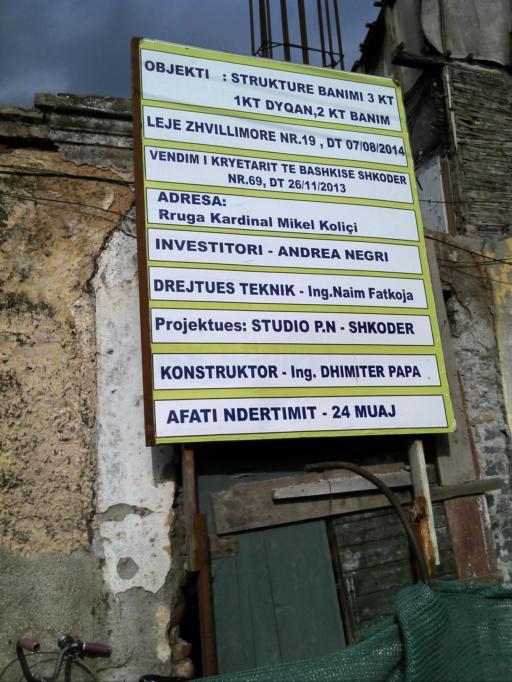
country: AL
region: Shkoder
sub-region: Rrethi i Shkodres
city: Shkoder
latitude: 42.0724
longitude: 19.5204
